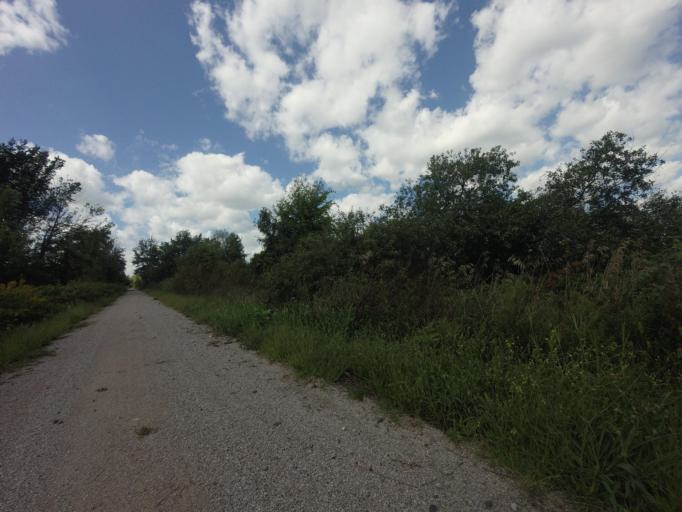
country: CA
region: Ontario
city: Huron East
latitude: 43.6213
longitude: -81.1567
